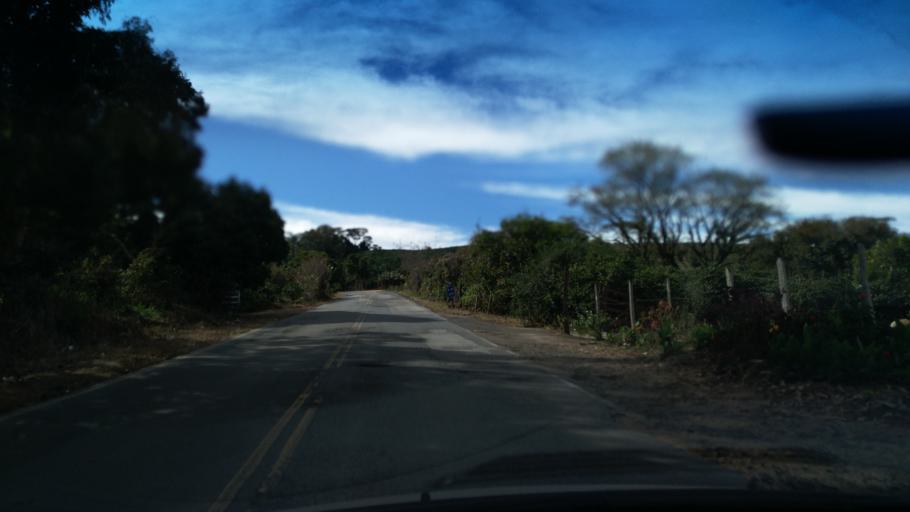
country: BR
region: Minas Gerais
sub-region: Andradas
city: Andradas
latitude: -22.0597
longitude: -46.3705
